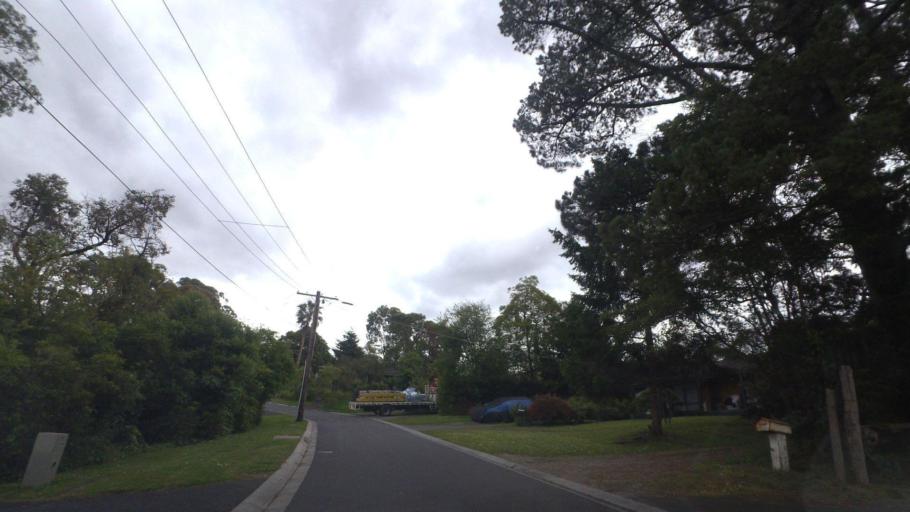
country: AU
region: Victoria
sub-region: Yarra Ranges
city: Mount Evelyn
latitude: -37.7864
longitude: 145.3741
